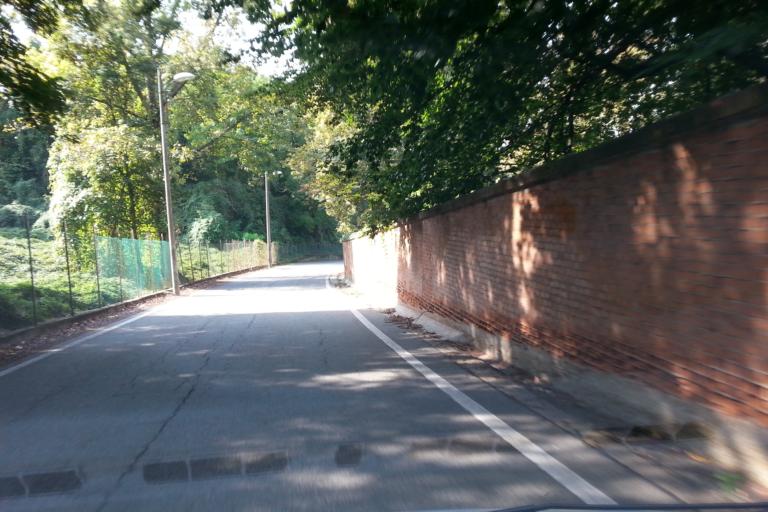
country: IT
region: Piedmont
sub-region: Provincia di Torino
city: Turin
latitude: 45.0432
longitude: 7.6889
